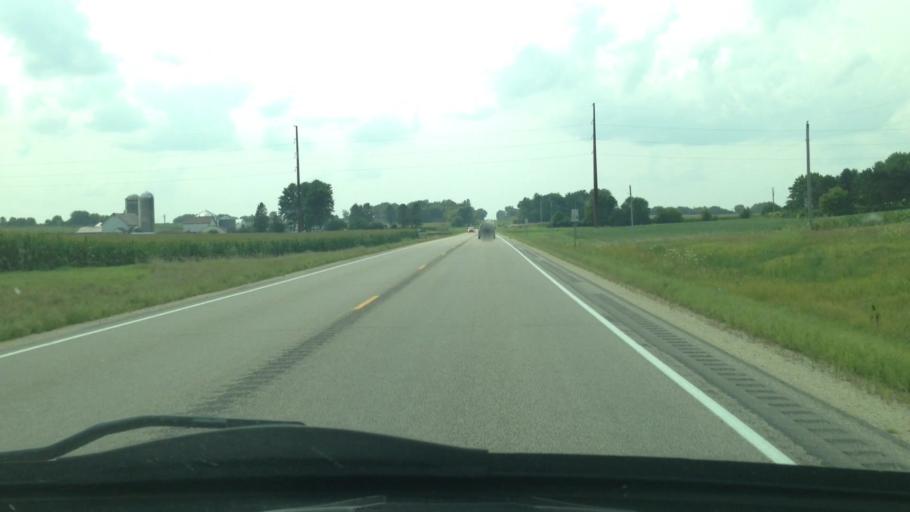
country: US
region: Minnesota
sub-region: Wabasha County
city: Elgin
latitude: 44.1658
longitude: -92.3749
